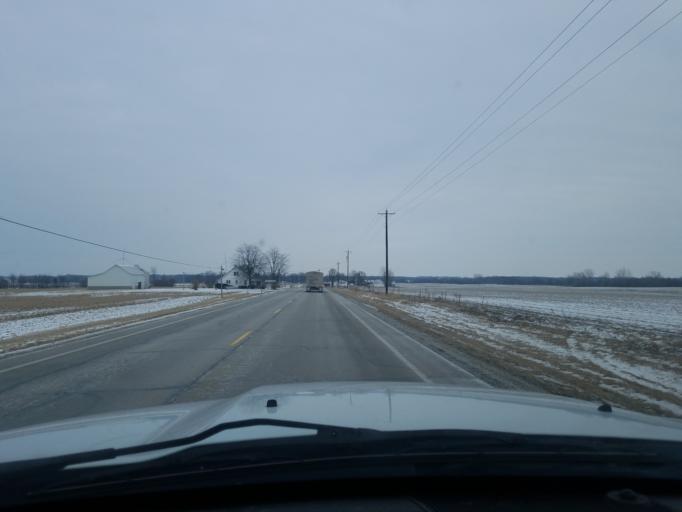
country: US
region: Indiana
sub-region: Randolph County
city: Lynn
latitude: 40.0486
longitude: -84.9908
